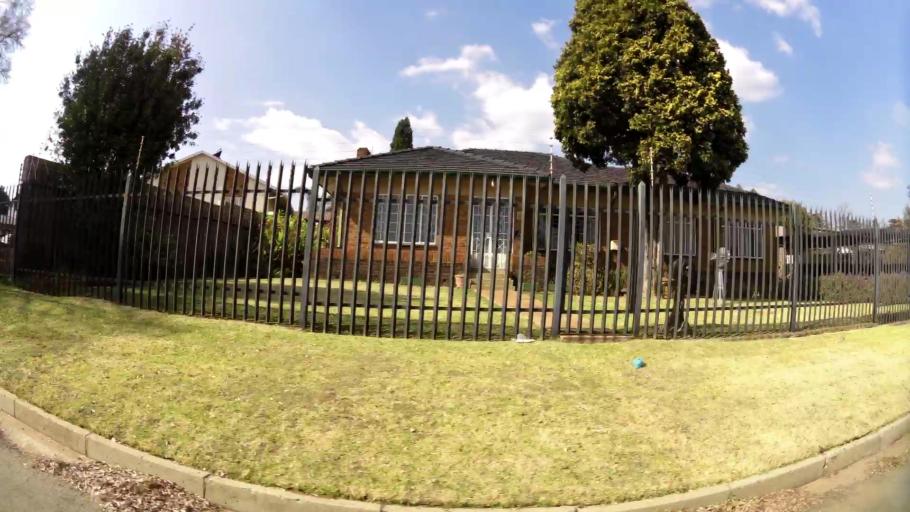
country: ZA
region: Gauteng
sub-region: City of Johannesburg Metropolitan Municipality
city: Modderfontein
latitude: -26.0850
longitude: 28.2234
